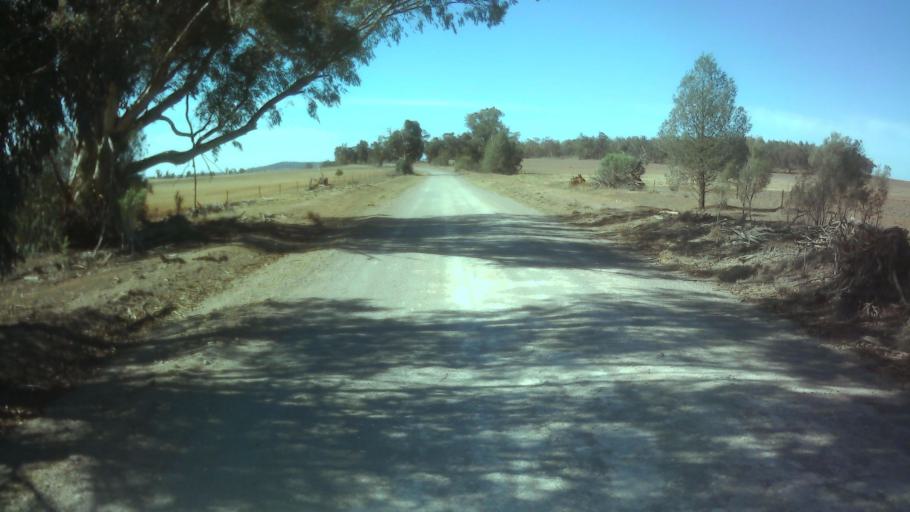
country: AU
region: New South Wales
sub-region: Forbes
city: Forbes
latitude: -33.7174
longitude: 147.7465
